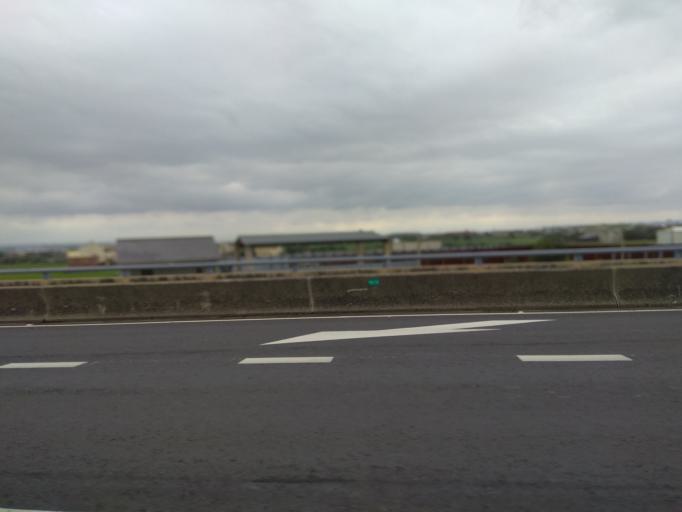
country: TW
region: Taiwan
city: Taoyuan City
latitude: 25.1078
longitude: 121.2236
